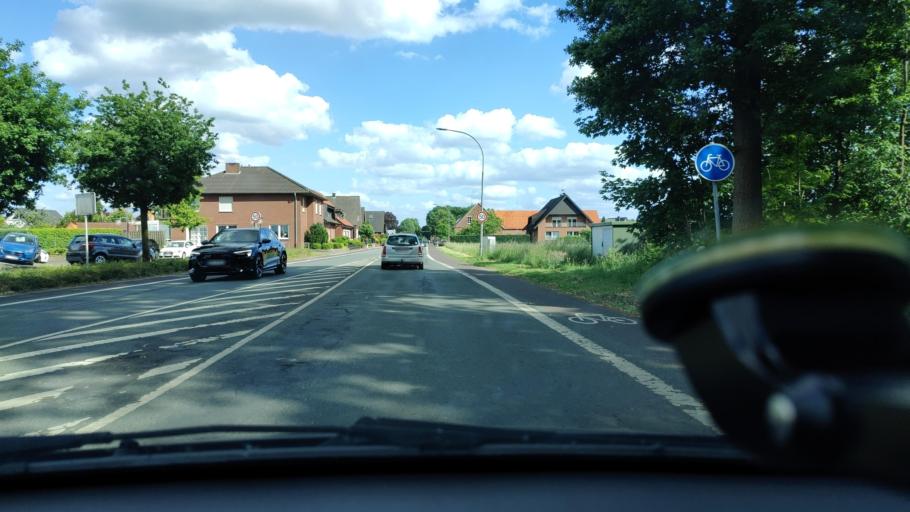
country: DE
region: North Rhine-Westphalia
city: Stadtlohn
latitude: 51.9887
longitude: 6.9382
